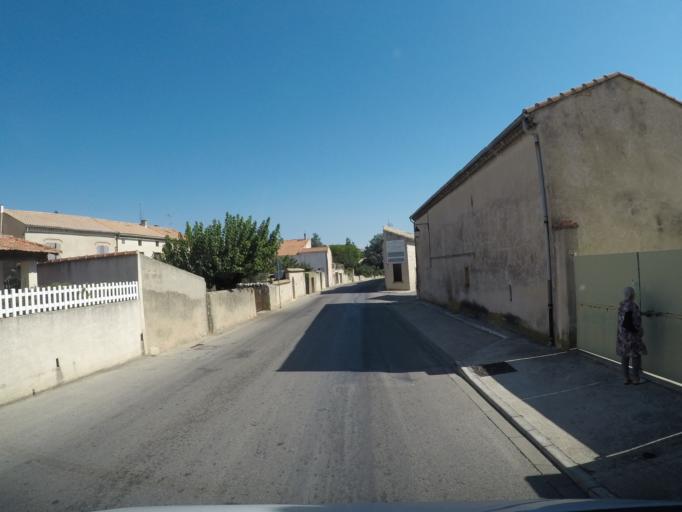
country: FR
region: Languedoc-Roussillon
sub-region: Departement du Gard
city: Tavel
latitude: 44.0123
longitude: 4.6967
